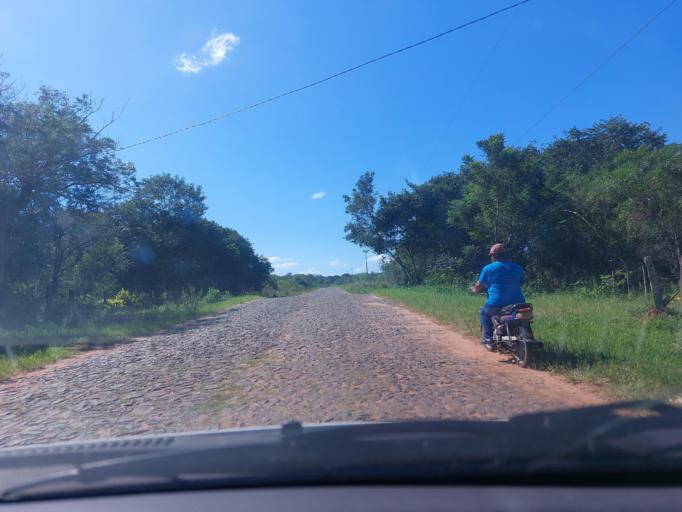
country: PY
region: San Pedro
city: Itacurubi del Rosario
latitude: -24.5888
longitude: -56.6020
